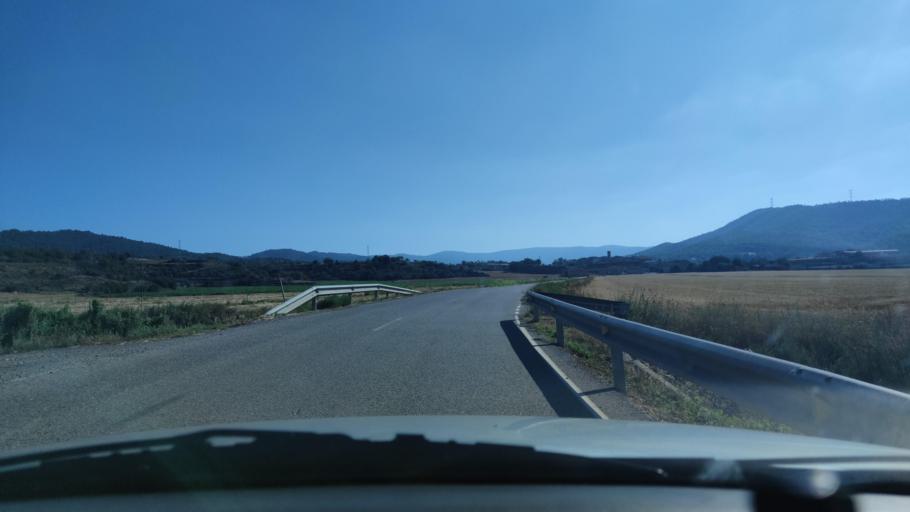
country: ES
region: Catalonia
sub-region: Provincia de Lleida
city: Ponts
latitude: 41.9071
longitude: 1.2440
